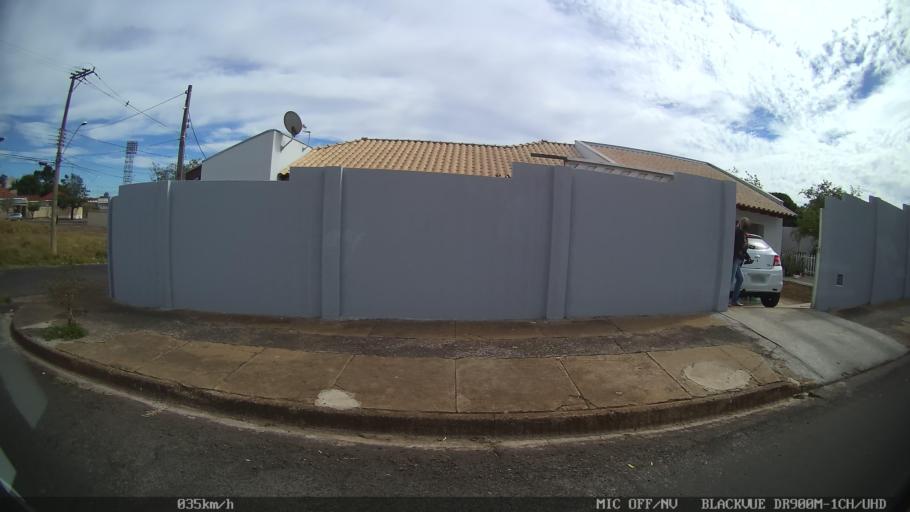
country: BR
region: Sao Paulo
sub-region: Catanduva
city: Catanduva
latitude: -21.1523
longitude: -48.9736
